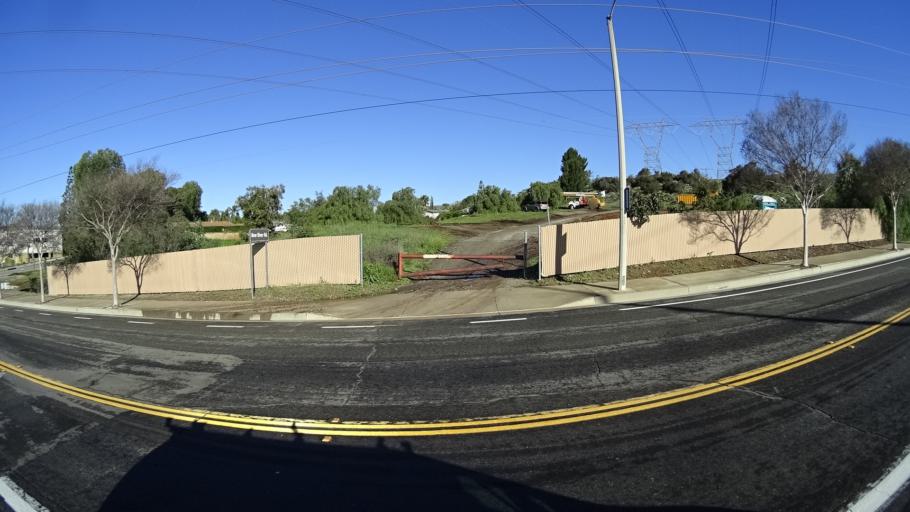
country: US
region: California
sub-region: Orange County
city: Yorba Linda
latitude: 33.8779
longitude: -117.7492
